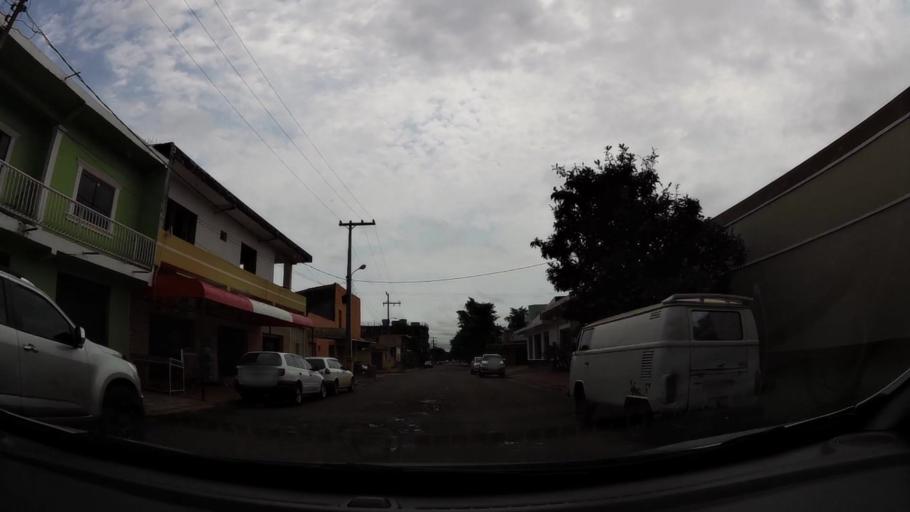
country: PY
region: Alto Parana
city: Ciudad del Este
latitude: -25.5021
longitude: -54.6657
